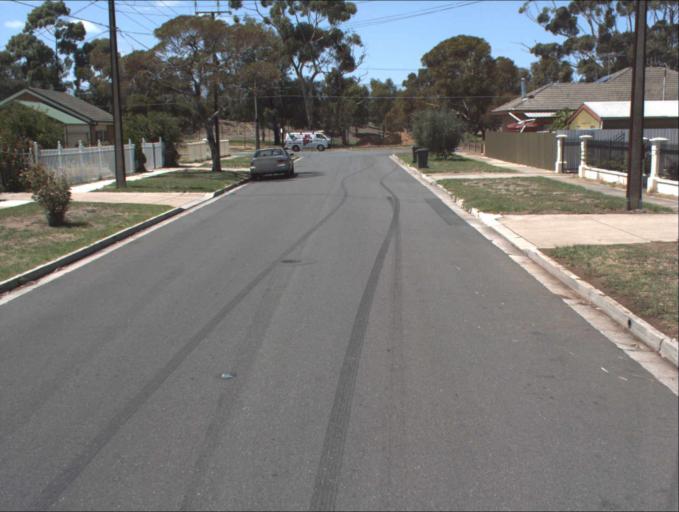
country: AU
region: South Australia
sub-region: Charles Sturt
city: Woodville North
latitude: -34.8617
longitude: 138.5645
